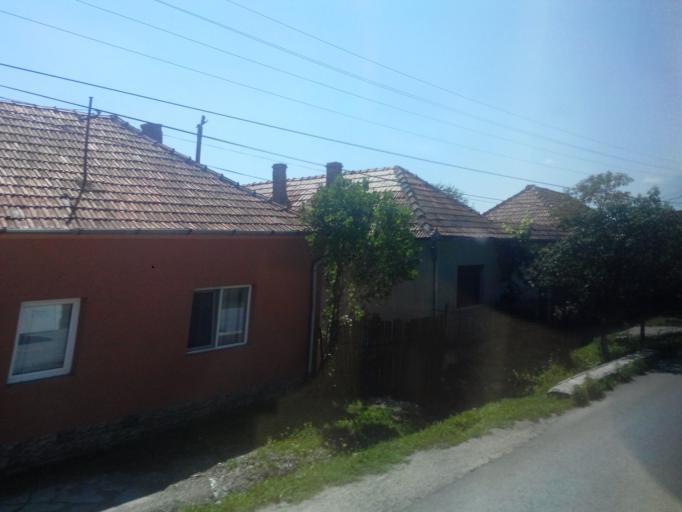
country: RO
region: Hunedoara
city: Lapugiu de Jos
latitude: 45.8873
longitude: 22.4533
